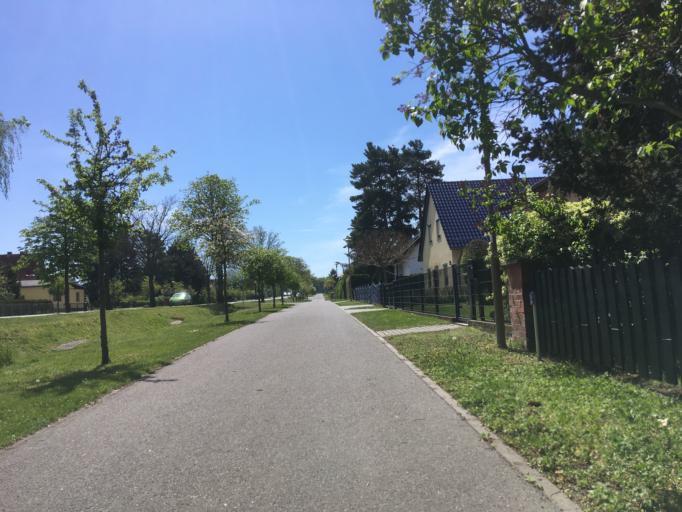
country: DE
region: Brandenburg
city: Wildau
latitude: 52.3346
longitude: 13.6089
